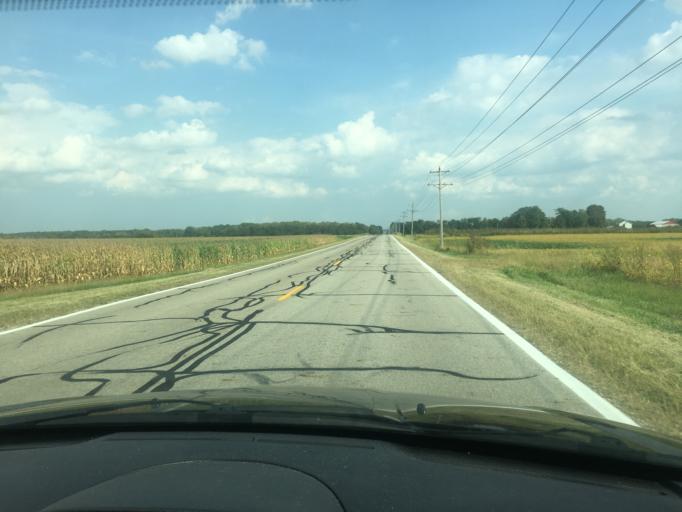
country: US
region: Ohio
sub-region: Champaign County
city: Urbana
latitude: 40.1309
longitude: -83.8244
